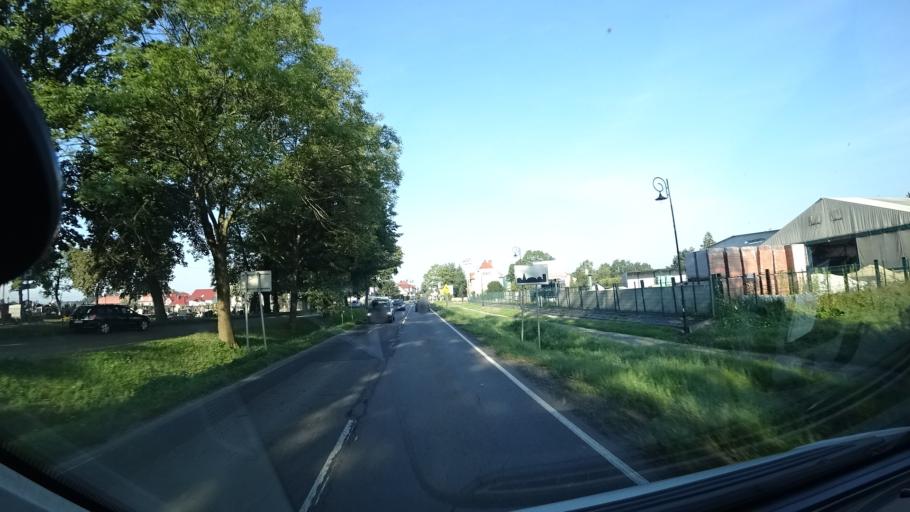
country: PL
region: Silesian Voivodeship
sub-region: Powiat gliwicki
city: Sosnicowice
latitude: 50.2704
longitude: 18.5368
